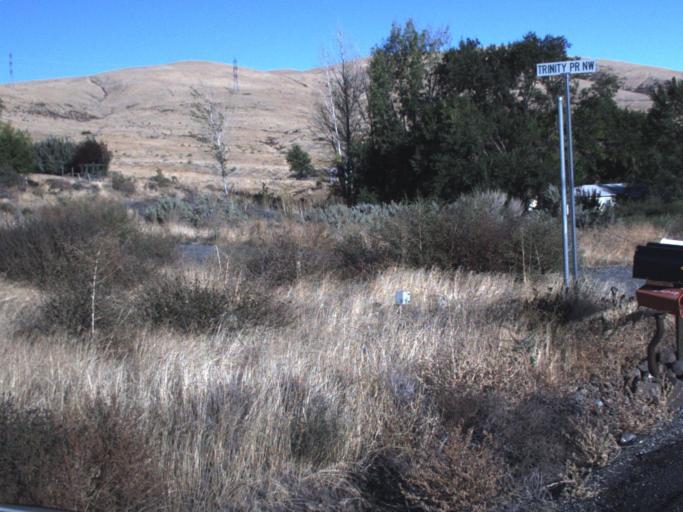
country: US
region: Washington
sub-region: Benton County
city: Benton City
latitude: 46.3201
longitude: -119.4932
